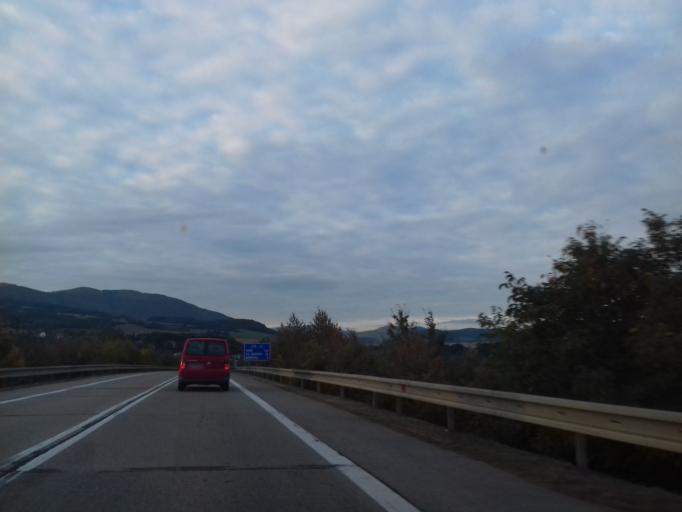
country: SK
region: Trenciansky
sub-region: Okres Trencin
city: Trencin
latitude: 48.8644
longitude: 17.9560
